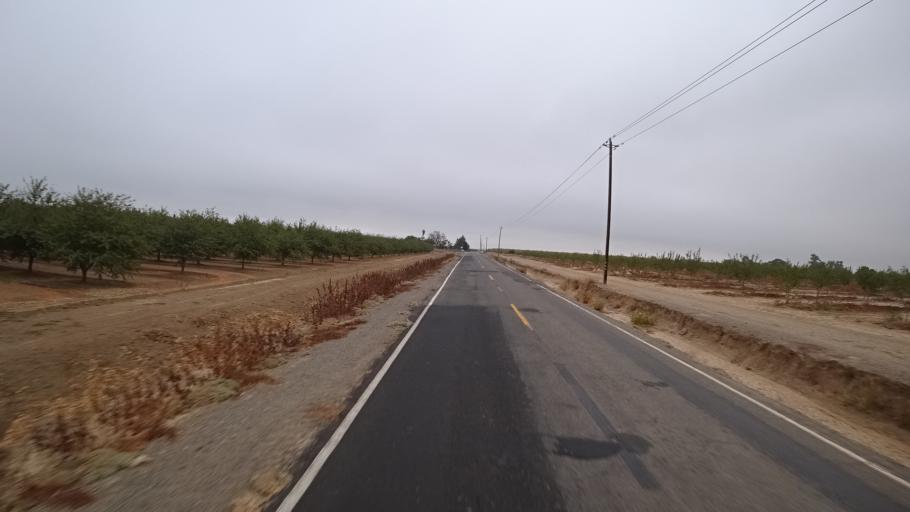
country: US
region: California
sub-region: Yolo County
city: Dunnigan
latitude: 38.9260
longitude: -122.0204
